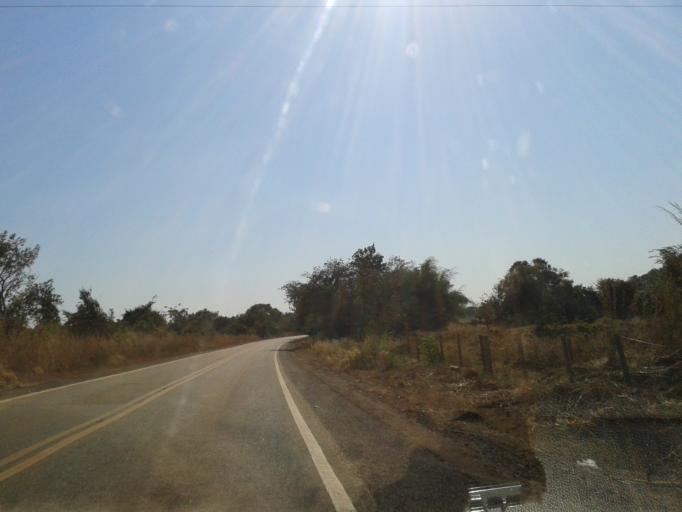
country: BR
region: Goias
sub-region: Mozarlandia
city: Mozarlandia
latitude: -14.6600
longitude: -50.5294
